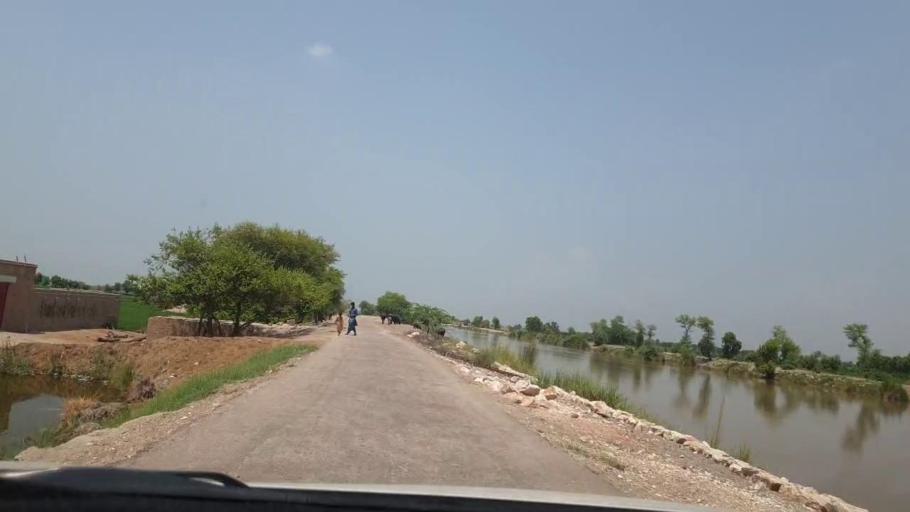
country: PK
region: Sindh
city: Dokri
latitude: 27.3300
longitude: 68.1094
